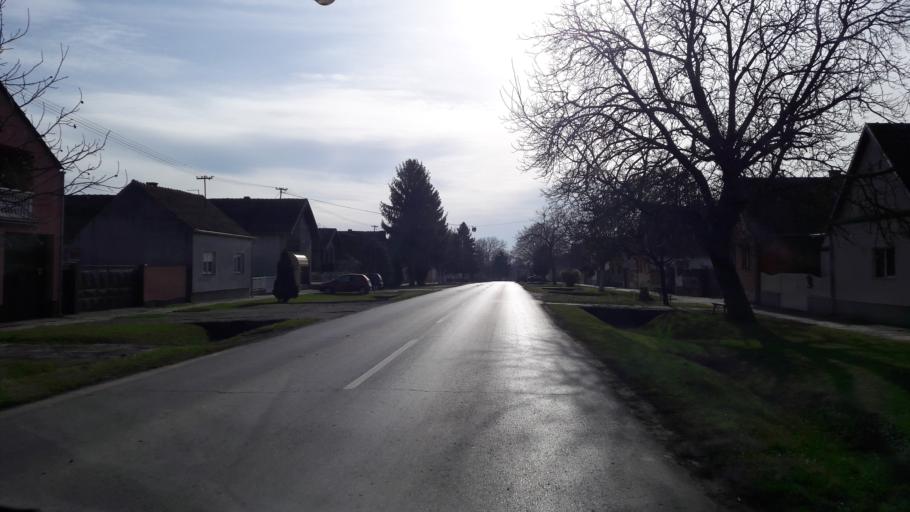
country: HR
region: Vukovarsko-Srijemska
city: Vodinci
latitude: 45.3036
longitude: 18.5598
